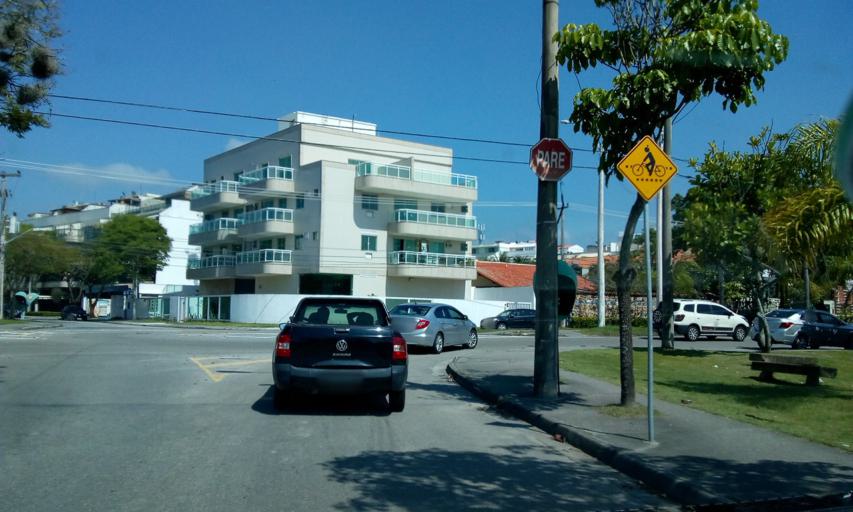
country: BR
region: Rio de Janeiro
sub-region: Nilopolis
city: Nilopolis
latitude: -23.0175
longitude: -43.4643
